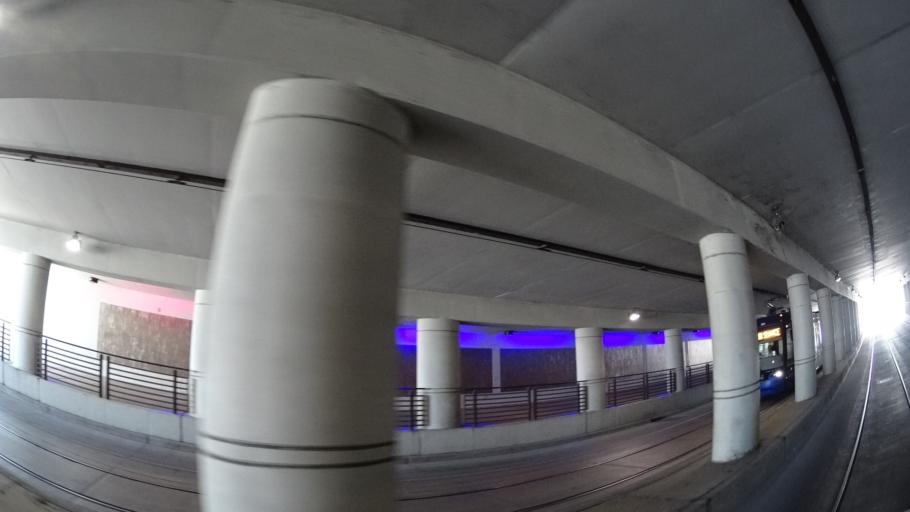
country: US
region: Arizona
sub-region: Pima County
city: South Tucson
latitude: 32.2233
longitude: -110.9657
